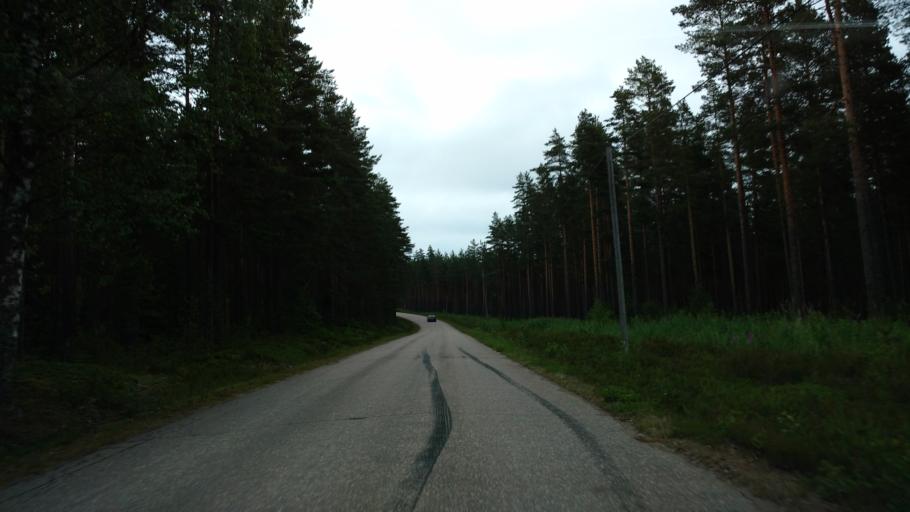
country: FI
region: Varsinais-Suomi
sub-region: Salo
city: Kiikala
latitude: 60.4462
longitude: 23.6274
